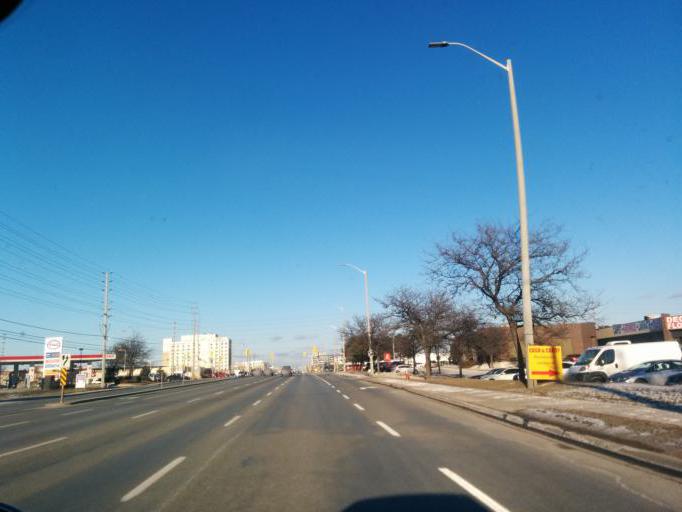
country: CA
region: Ontario
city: Etobicoke
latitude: 43.6345
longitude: -79.6219
